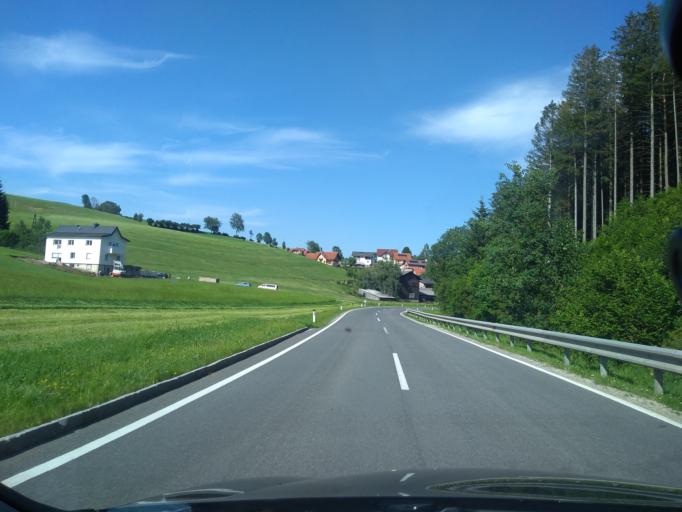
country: AT
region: Styria
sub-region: Politischer Bezirk Weiz
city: Passail
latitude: 47.2713
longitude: 15.4563
